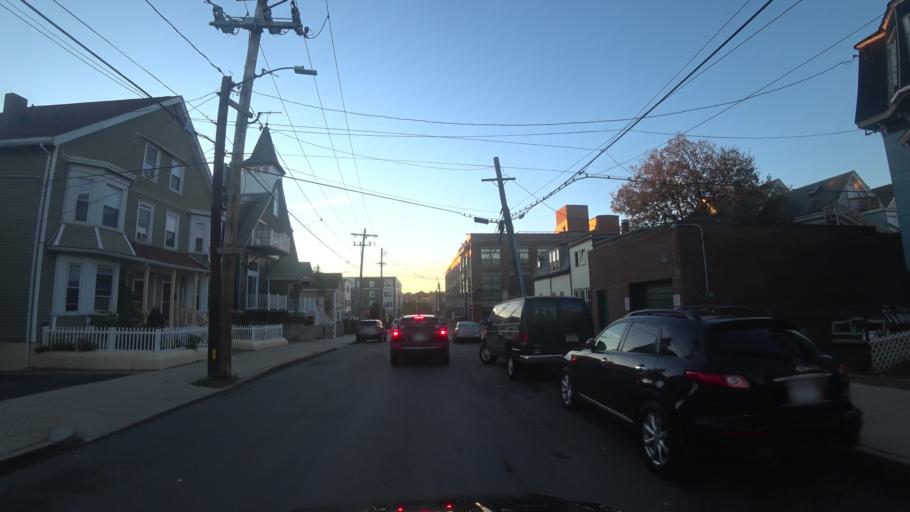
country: US
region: Massachusetts
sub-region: Suffolk County
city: Chelsea
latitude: 42.3995
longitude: -71.0221
